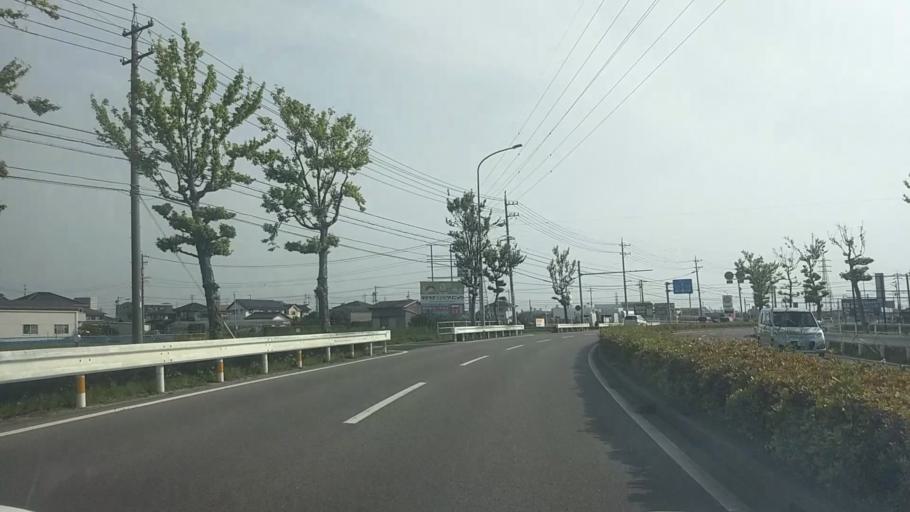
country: JP
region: Aichi
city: Anjo
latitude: 34.9683
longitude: 137.0737
